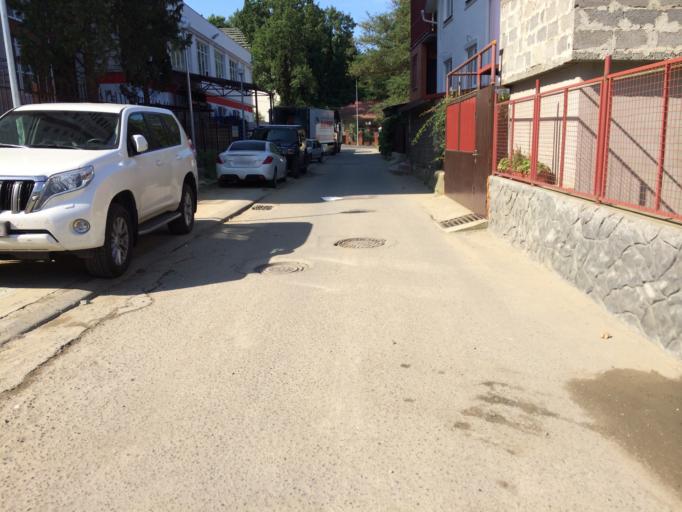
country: RU
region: Krasnodarskiy
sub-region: Sochi City
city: Sochi
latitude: 43.5913
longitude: 39.7322
